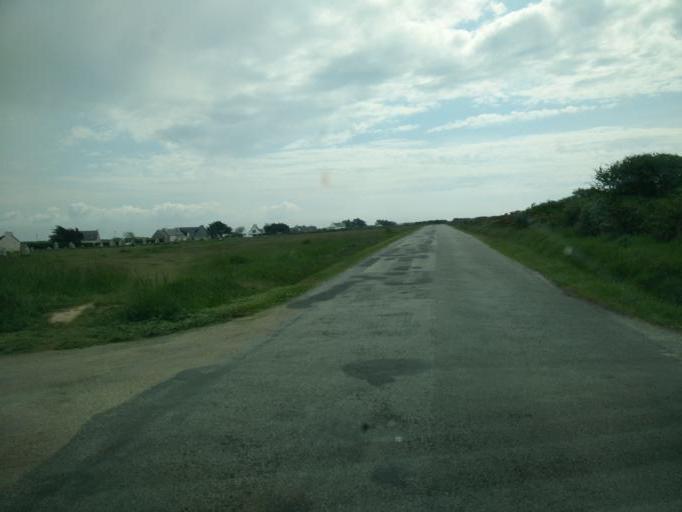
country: FR
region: Brittany
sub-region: Departement du Finistere
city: Camaret-sur-Mer
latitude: 48.2747
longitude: -4.6100
